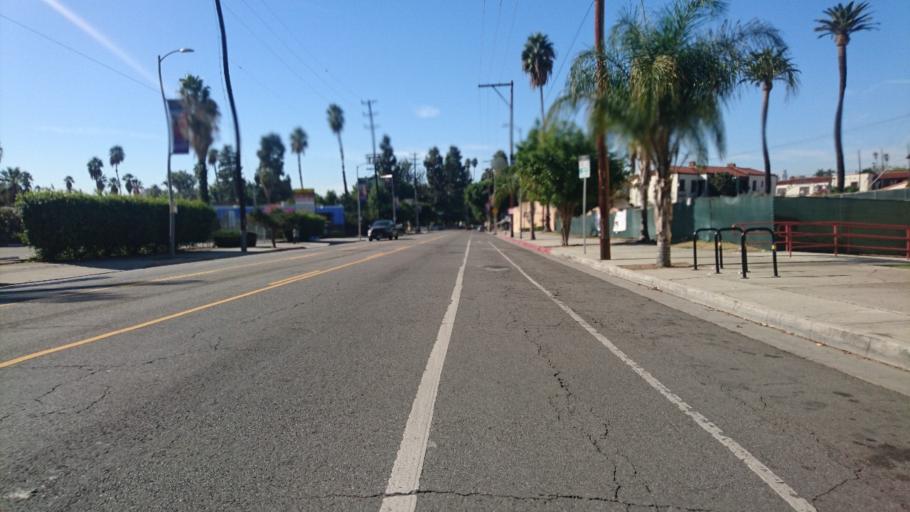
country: US
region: California
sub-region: Los Angeles County
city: Boyle Heights
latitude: 34.0701
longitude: -118.1994
